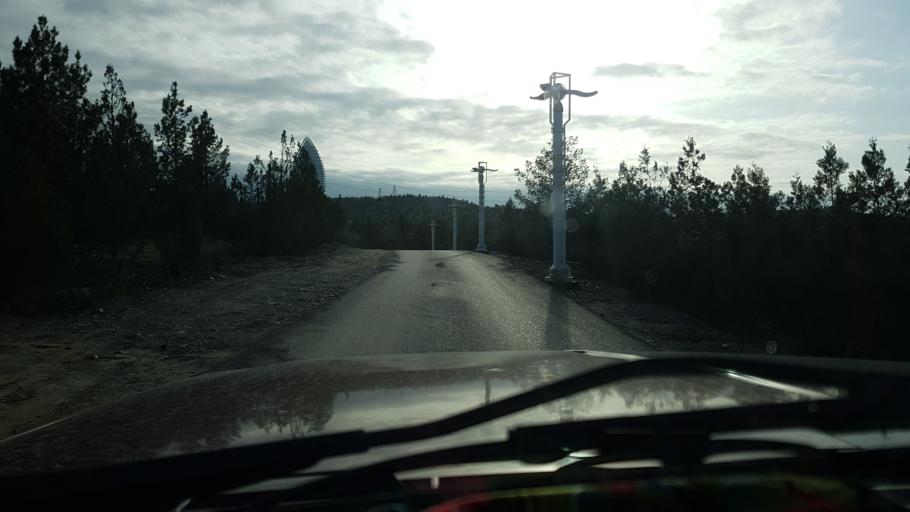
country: TM
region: Ahal
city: Ashgabat
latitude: 37.9348
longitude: 58.3457
